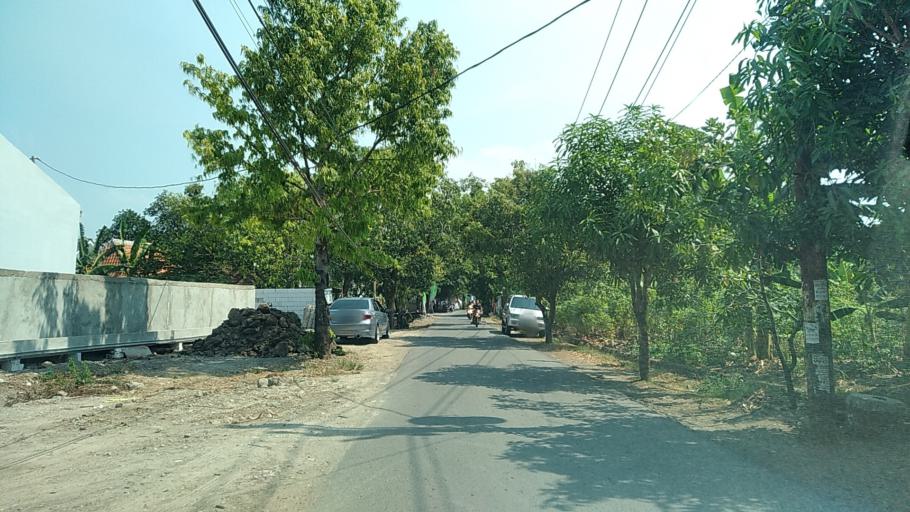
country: ID
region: Central Java
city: Mranggen
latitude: -7.0500
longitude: 110.4806
